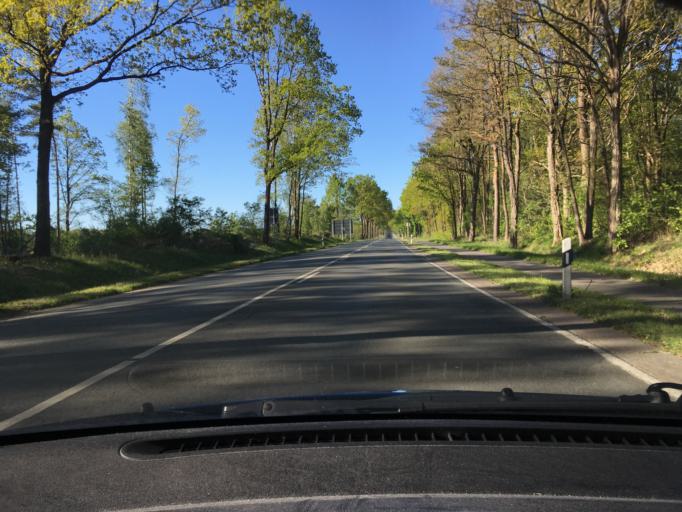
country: DE
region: Lower Saxony
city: Soltau
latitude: 53.0281
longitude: 9.8511
